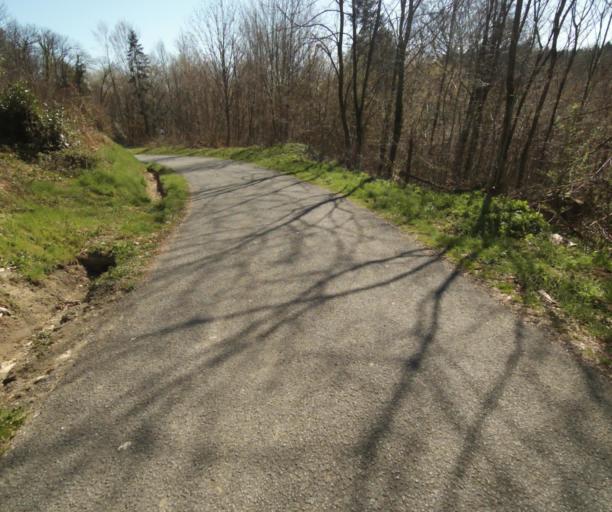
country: FR
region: Limousin
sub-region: Departement de la Correze
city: Saint-Mexant
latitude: 45.3088
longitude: 1.6350
